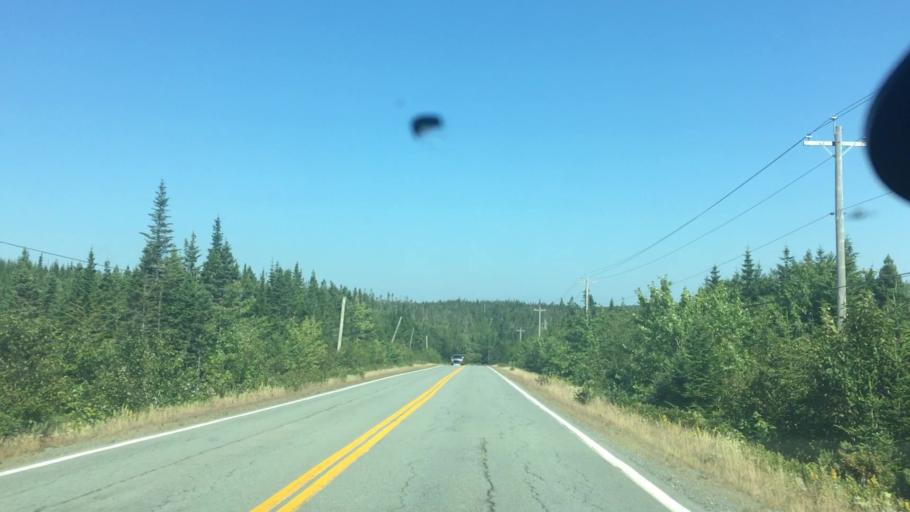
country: CA
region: Nova Scotia
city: Antigonish
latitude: 45.0106
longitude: -62.1055
